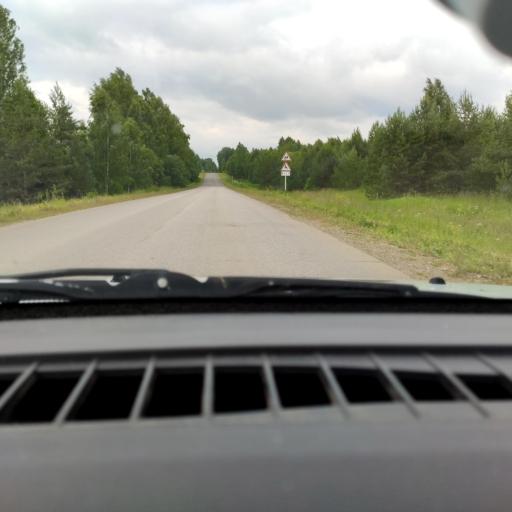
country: RU
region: Perm
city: Orda
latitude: 57.1375
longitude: 56.7188
